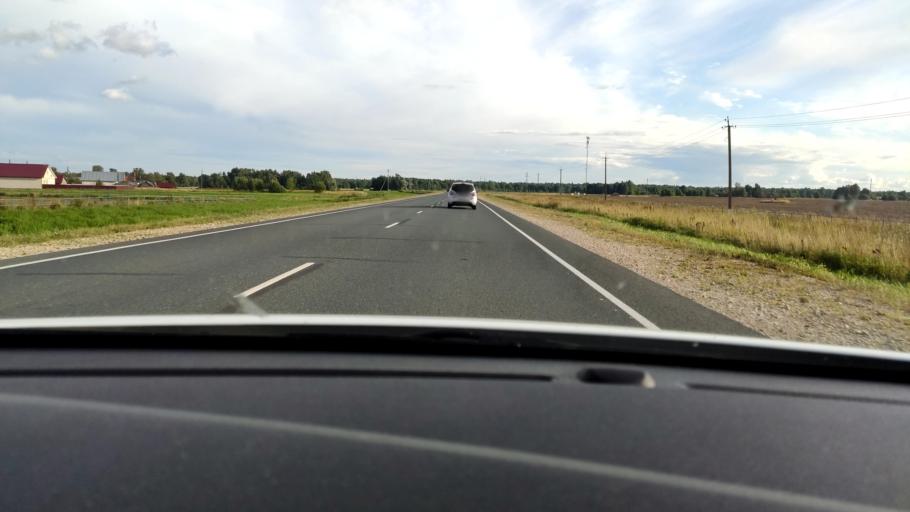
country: RU
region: Mariy-El
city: Krasnogorskiy
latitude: 56.2024
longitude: 48.2357
